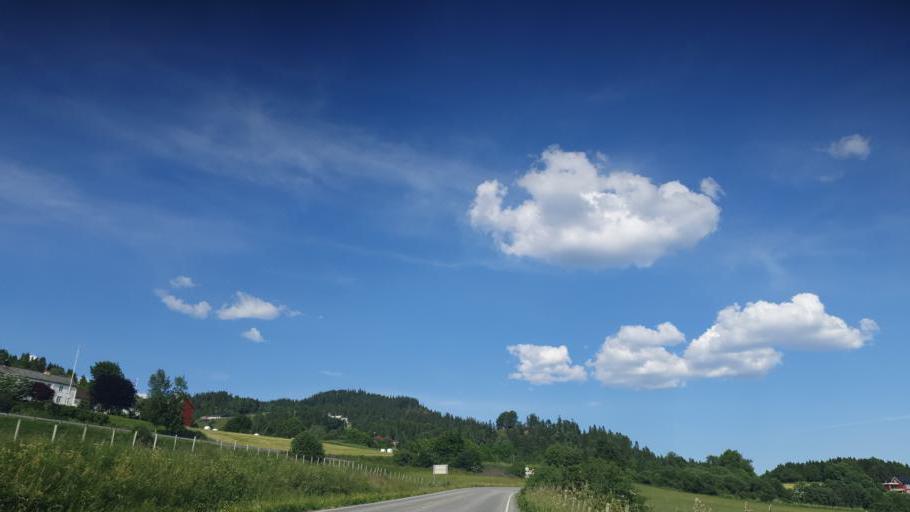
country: NO
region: Nord-Trondelag
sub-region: Leksvik
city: Leksvik
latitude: 63.6764
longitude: 10.6358
